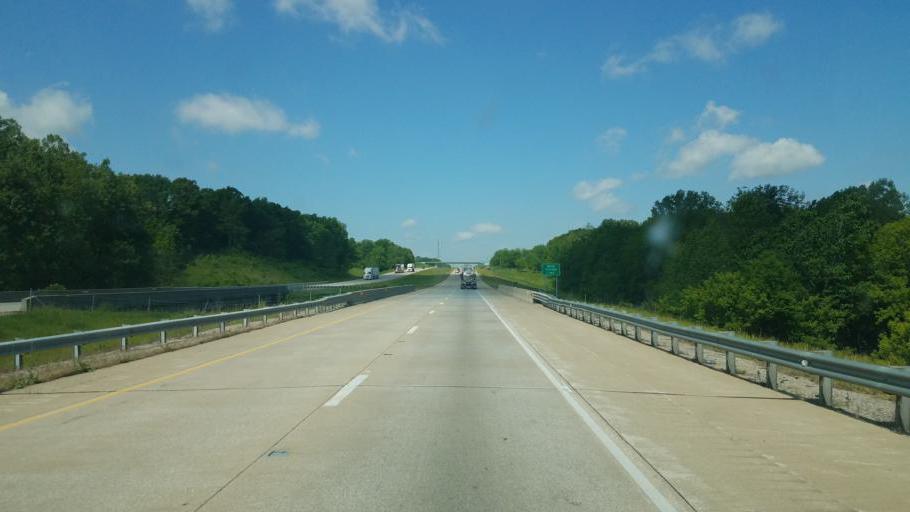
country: US
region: Illinois
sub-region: Clark County
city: Marshall
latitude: 39.4258
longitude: -87.5913
